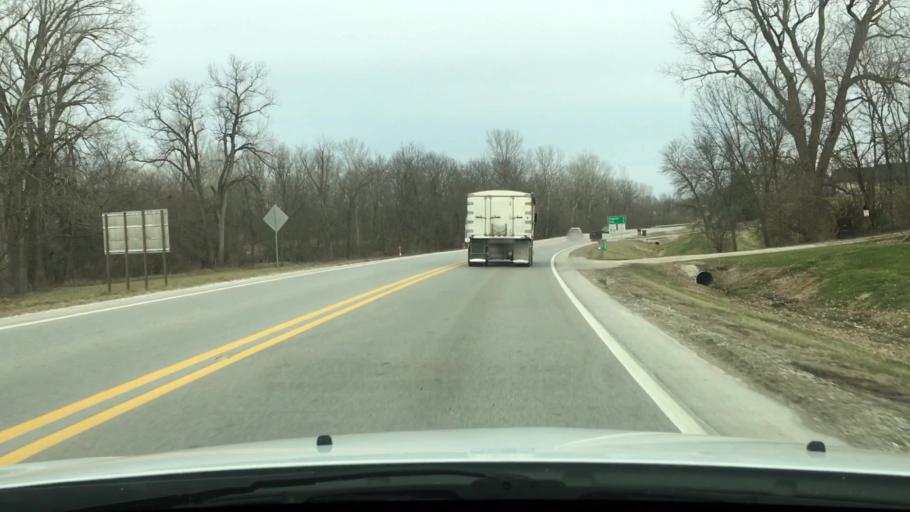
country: US
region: Illinois
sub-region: Pike County
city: Pittsfield
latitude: 39.6233
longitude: -90.7997
